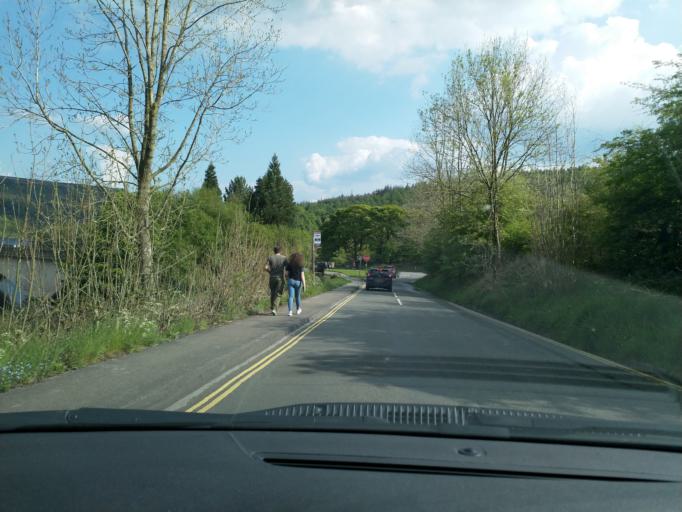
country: GB
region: England
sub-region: Derbyshire
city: Hope Valley
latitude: 53.3755
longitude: -1.7141
